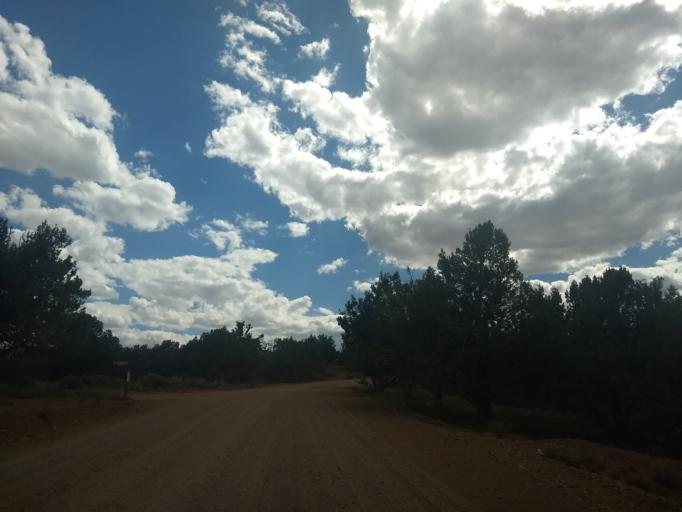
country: US
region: Utah
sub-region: Kane County
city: Kanab
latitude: 37.1479
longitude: -112.5457
